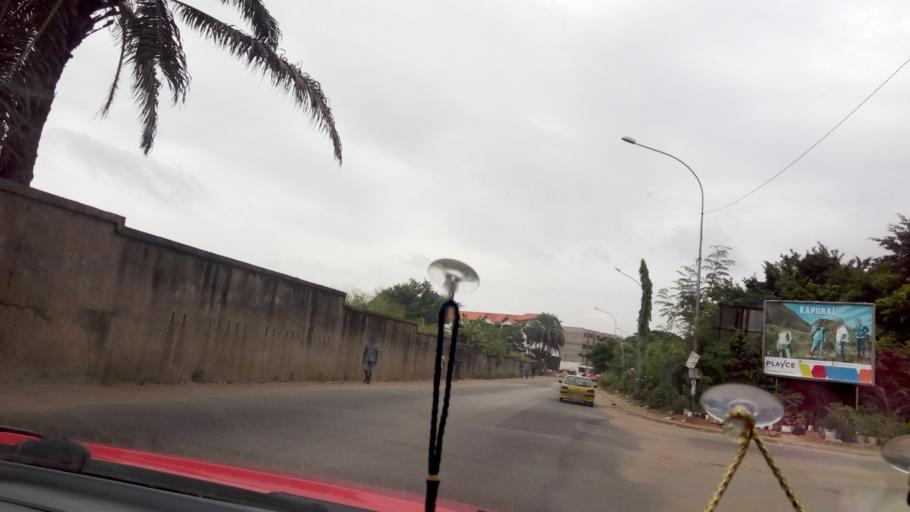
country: CI
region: Lagunes
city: Abidjan
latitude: 5.3441
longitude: -3.9745
